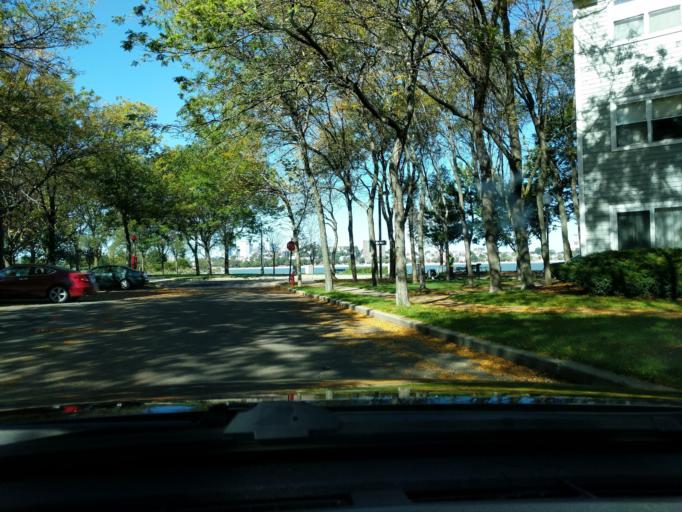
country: US
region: Massachusetts
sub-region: Suffolk County
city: South Boston
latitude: 42.3208
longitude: -71.0428
